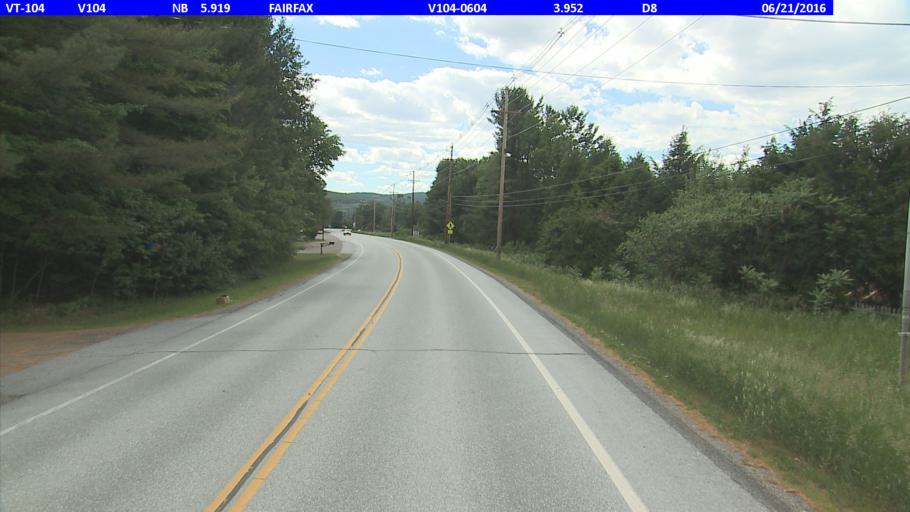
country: US
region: Vermont
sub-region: Chittenden County
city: Milton
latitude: 44.6535
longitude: -72.9984
